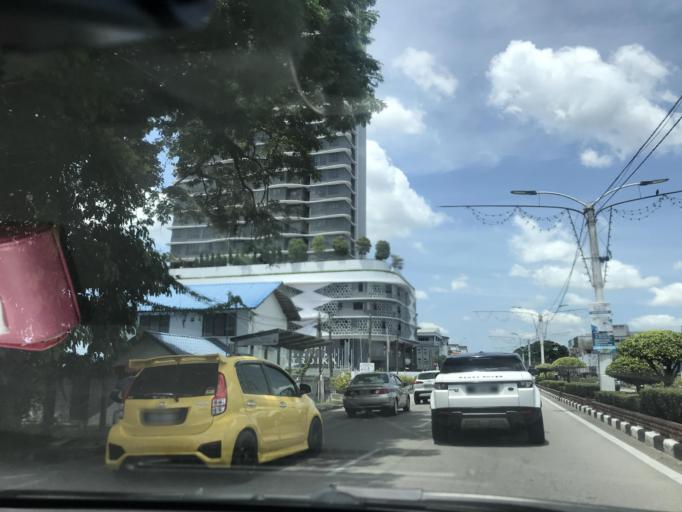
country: MY
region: Kelantan
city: Kota Bharu
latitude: 6.1213
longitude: 102.2399
